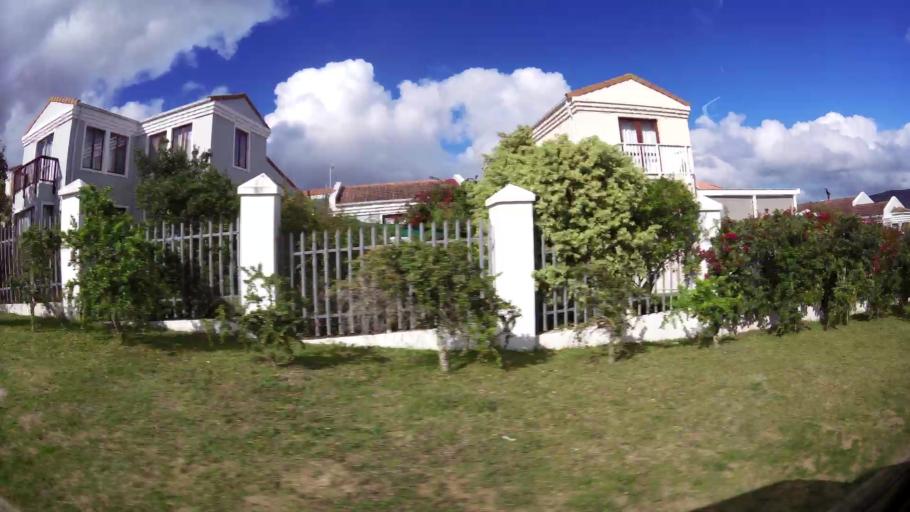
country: ZA
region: Western Cape
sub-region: Eden District Municipality
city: Knysna
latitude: -34.0529
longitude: 23.0776
